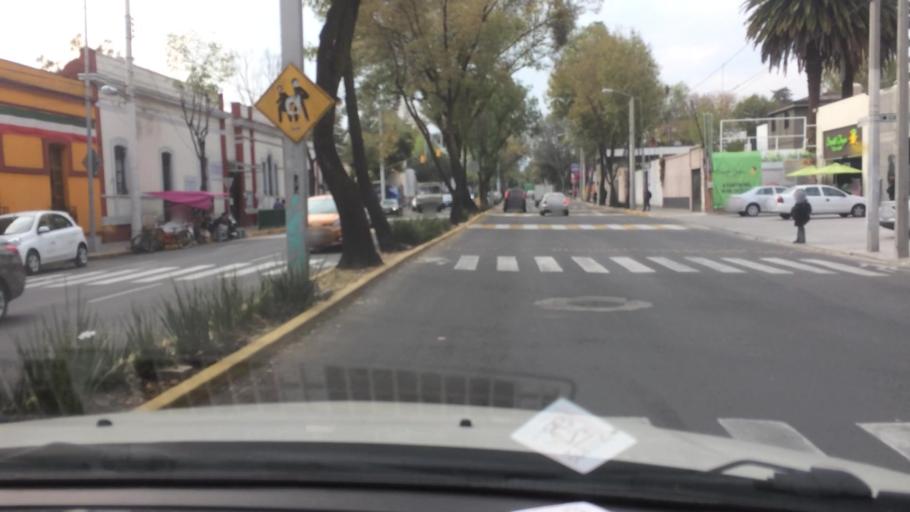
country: MX
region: Mexico City
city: Tlalpan
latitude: 19.2921
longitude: -99.1669
